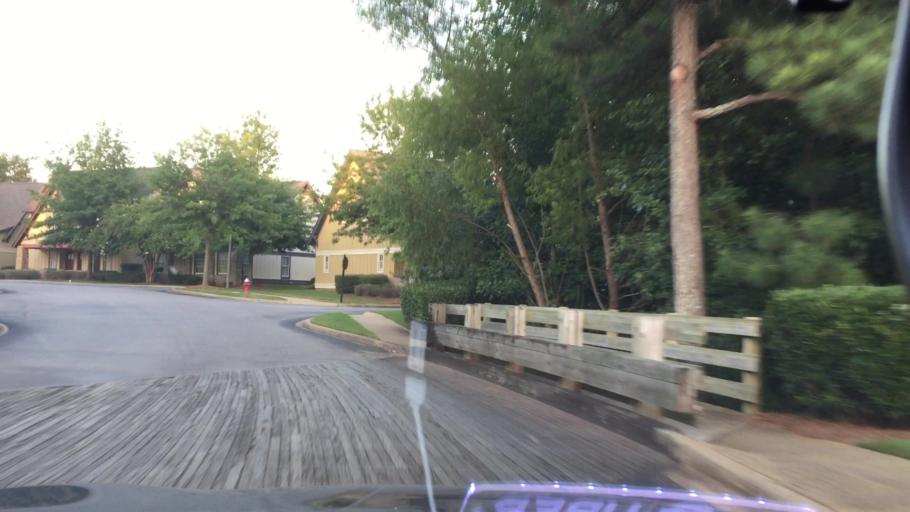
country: US
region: Alabama
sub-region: Lee County
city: Auburn
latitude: 32.6175
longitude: -85.4688
